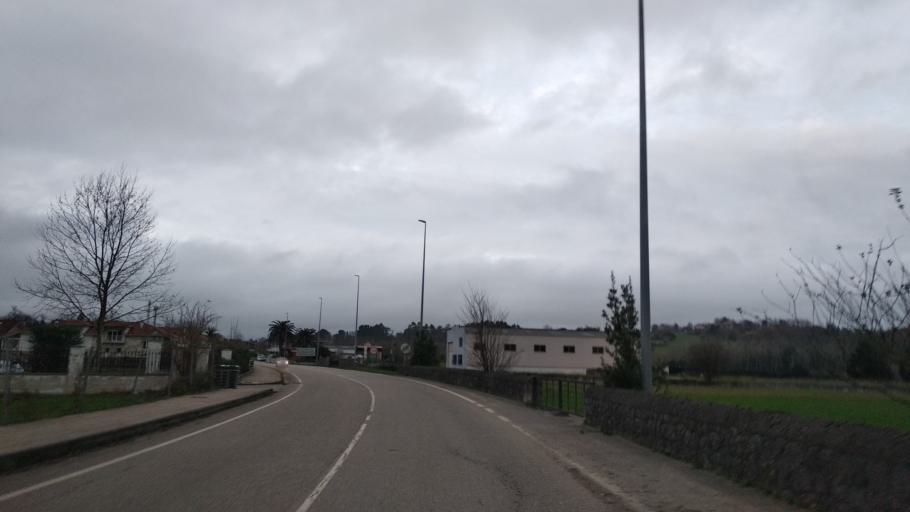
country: ES
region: Cantabria
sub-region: Provincia de Cantabria
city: Entrambasaguas
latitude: 43.4136
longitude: -3.6983
